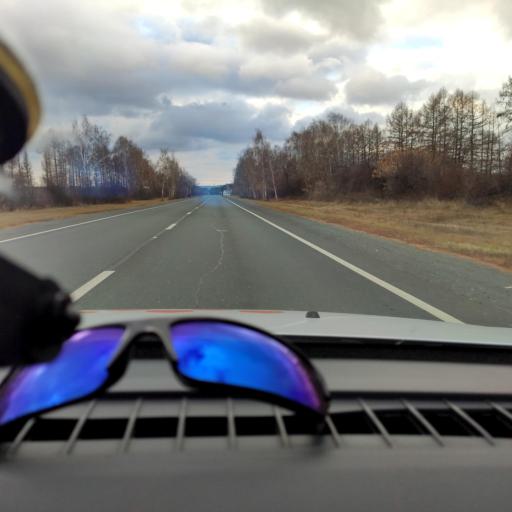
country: RU
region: Samara
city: Volzhskiy
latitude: 53.4625
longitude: 50.1275
